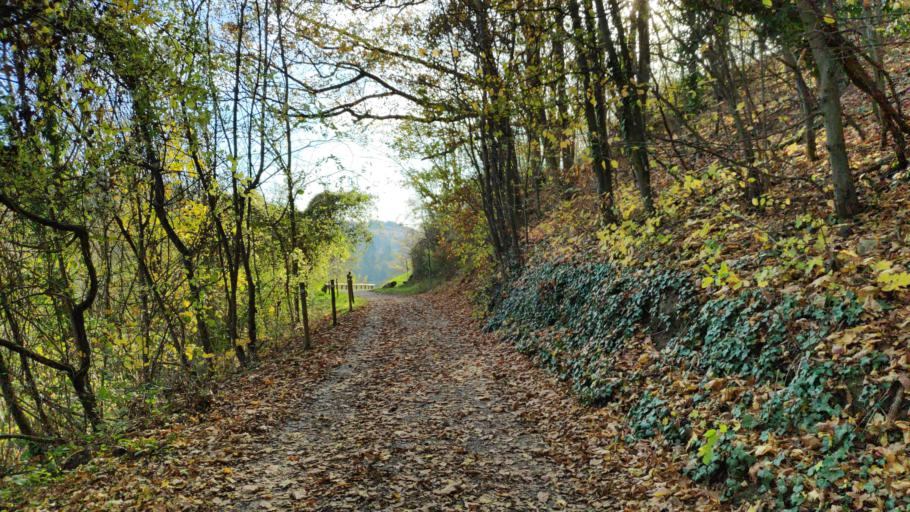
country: DE
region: Hesse
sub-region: Regierungsbezirk Darmstadt
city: Heppenheim an der Bergstrasse
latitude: 49.6464
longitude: 8.6520
